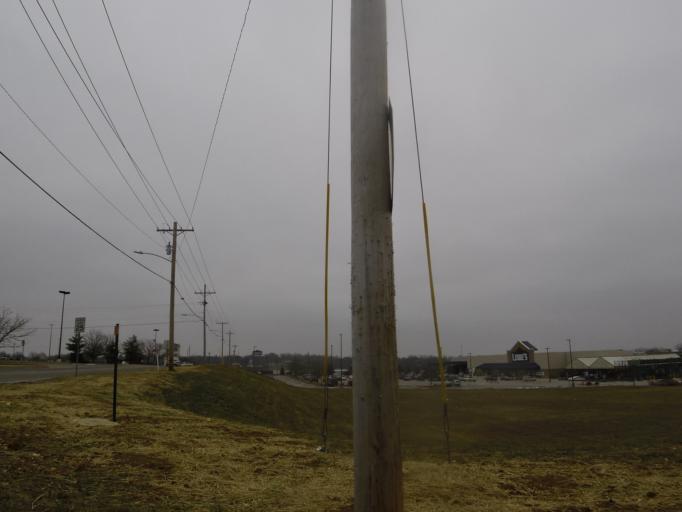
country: US
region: Missouri
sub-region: Marion County
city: Hannibal
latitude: 39.7225
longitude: -91.4015
